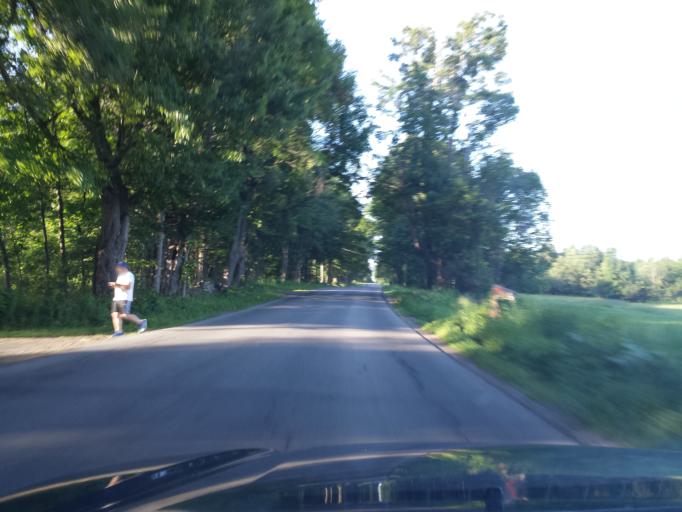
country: US
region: New York
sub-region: St. Lawrence County
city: Potsdam
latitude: 44.7013
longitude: -74.9654
